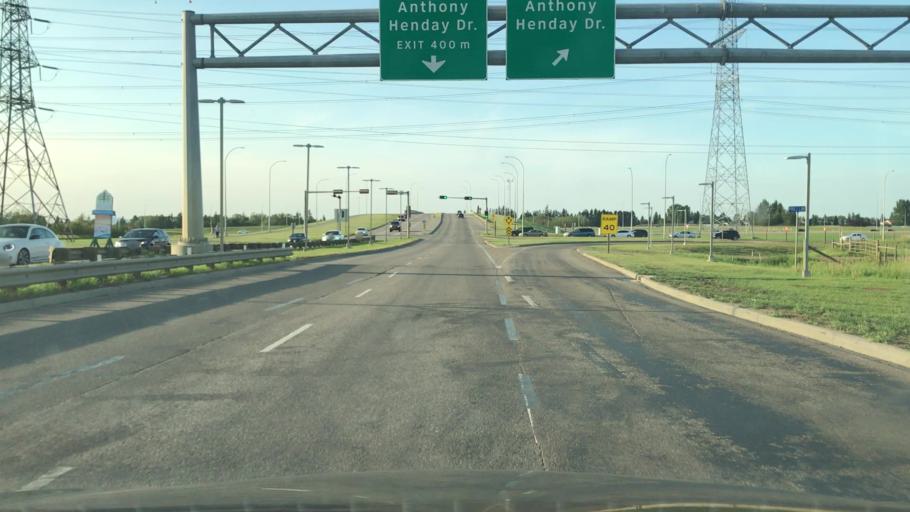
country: CA
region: Alberta
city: Beaumont
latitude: 53.4320
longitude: -113.4178
